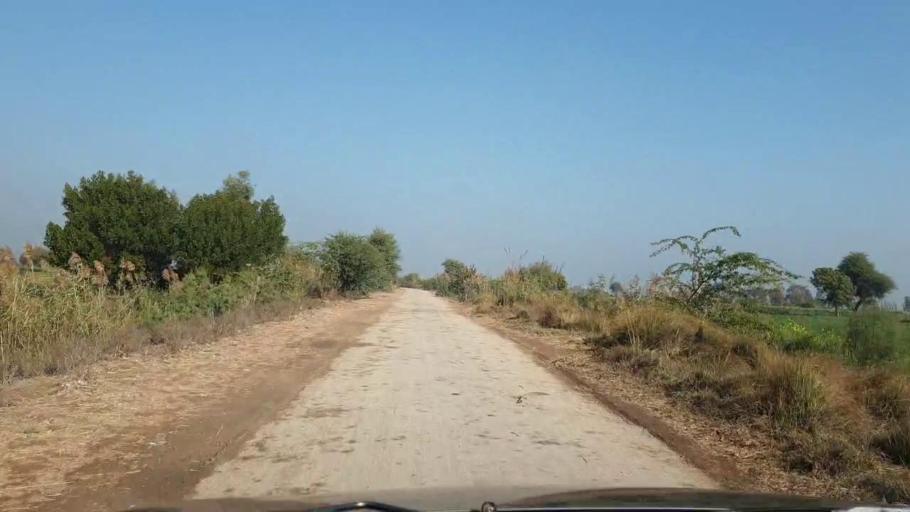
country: PK
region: Sindh
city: Sinjhoro
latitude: 26.0615
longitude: 68.7881
